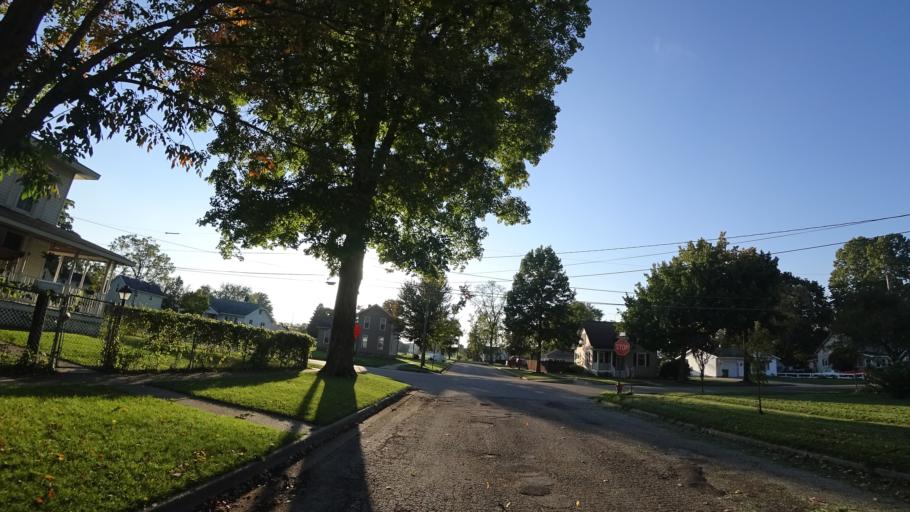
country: US
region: Michigan
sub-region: Saint Joseph County
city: Three Rivers
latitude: 41.9438
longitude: -85.6428
